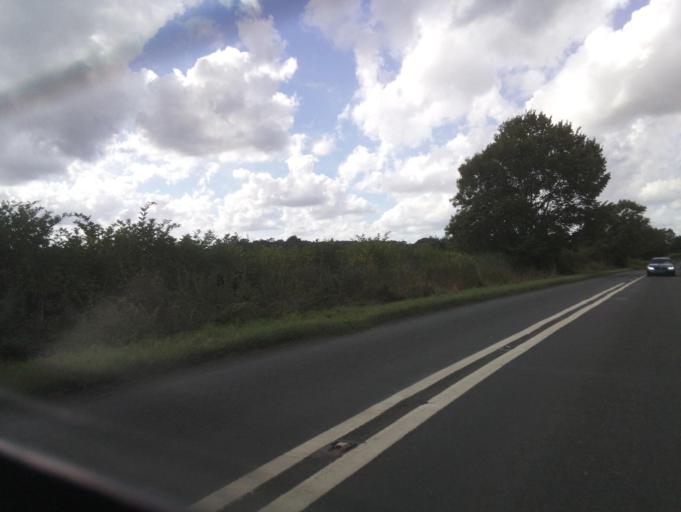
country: GB
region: England
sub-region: North Yorkshire
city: Bedale
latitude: 54.2383
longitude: -1.6796
